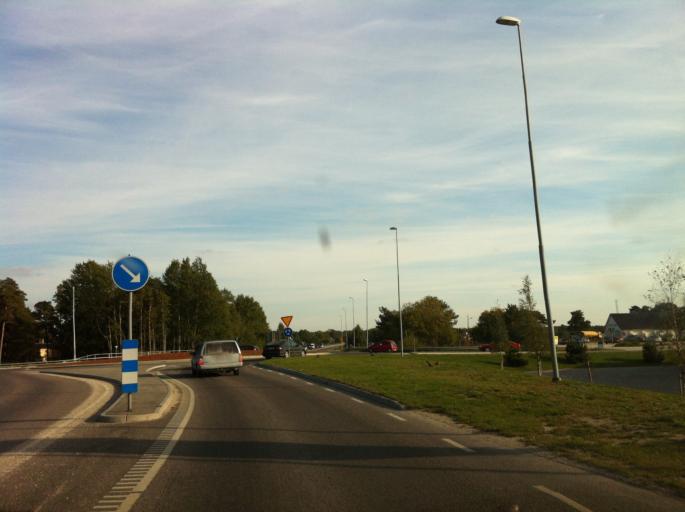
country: SE
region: Gotland
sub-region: Gotland
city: Visby
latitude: 57.6235
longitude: 18.3250
